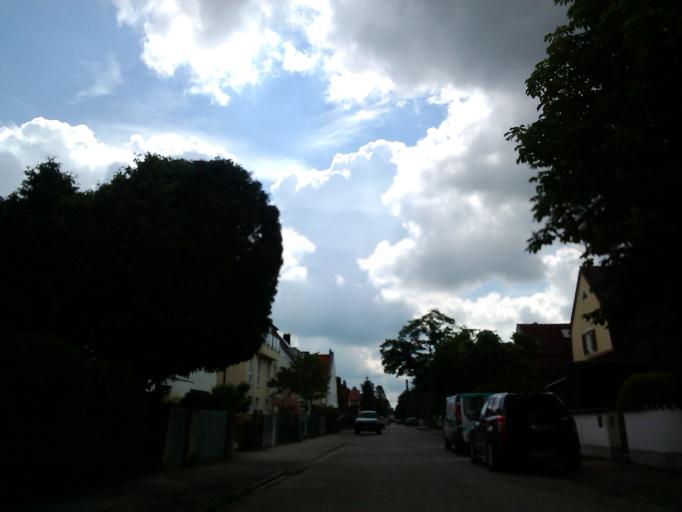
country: DE
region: Bavaria
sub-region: Upper Bavaria
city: Bogenhausen
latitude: 48.1226
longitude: 11.6476
